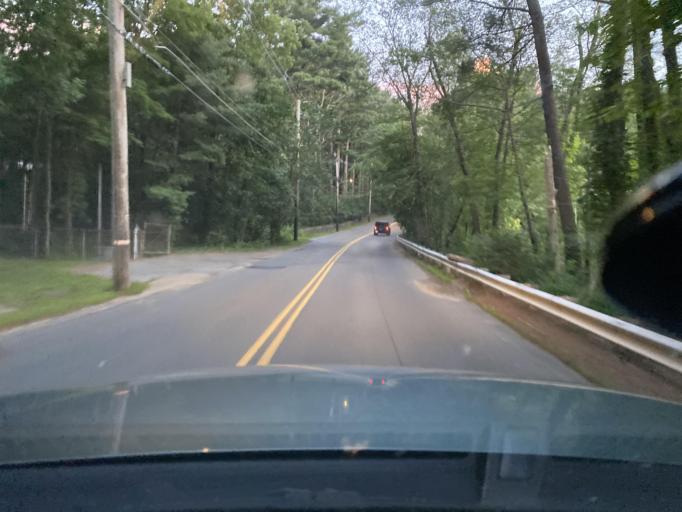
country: US
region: Massachusetts
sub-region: Essex County
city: Lynnfield
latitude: 42.5302
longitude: -70.9991
